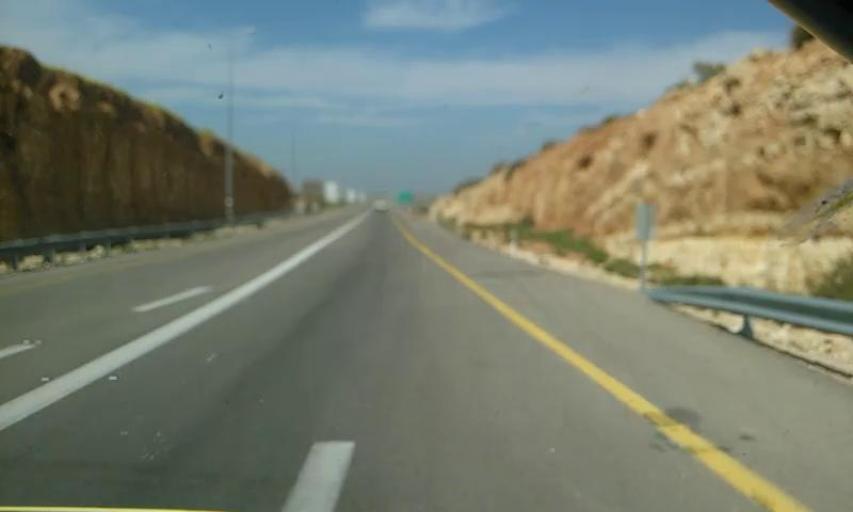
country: PS
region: West Bank
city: Az Zahiriyah
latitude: 31.3789
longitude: 35.0044
